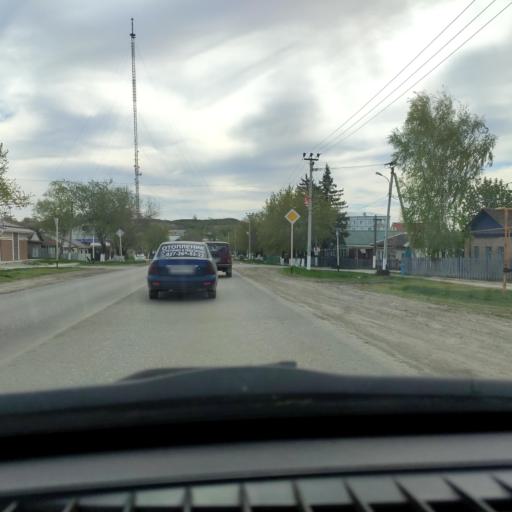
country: RU
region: Samara
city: Surgut
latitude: 53.9410
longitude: 51.1676
